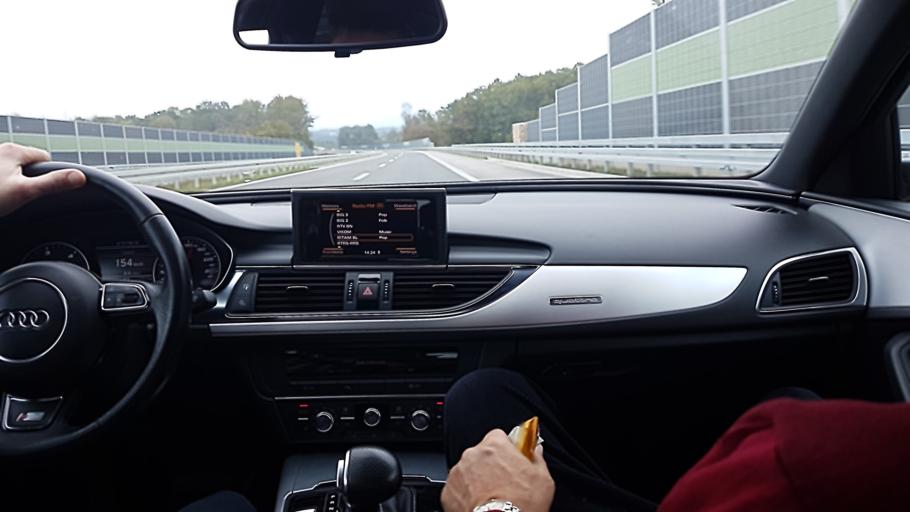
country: BA
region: Republika Srpska
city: Stanari
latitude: 44.8450
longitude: 17.7783
